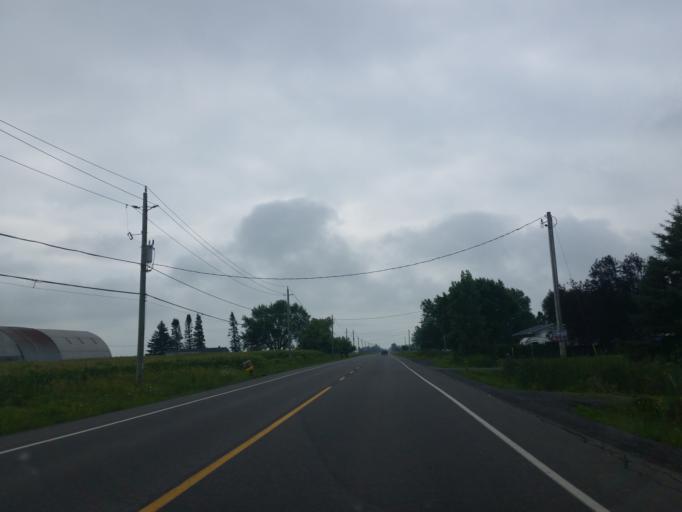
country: CA
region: Ontario
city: Clarence-Rockland
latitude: 45.4558
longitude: -75.4460
